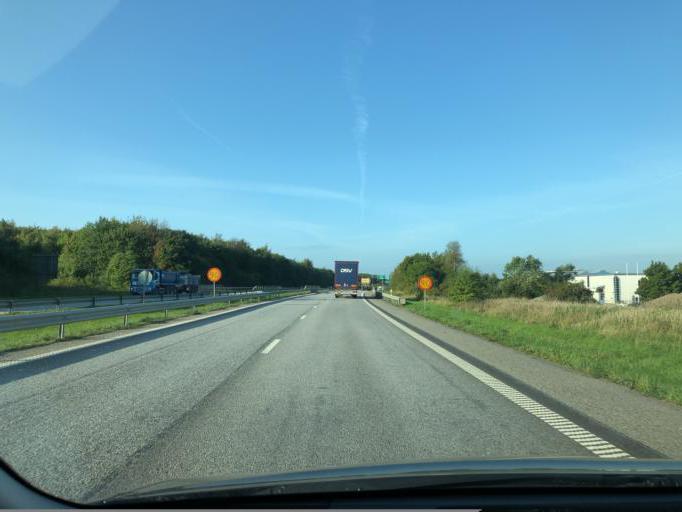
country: SE
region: Skane
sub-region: Burlovs Kommun
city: Arloev
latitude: 55.6056
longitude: 13.0781
